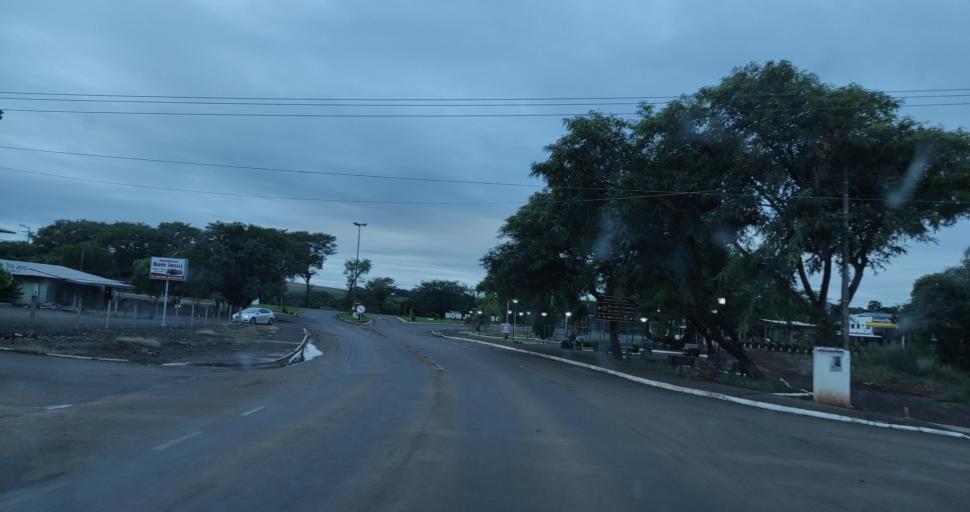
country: BR
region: Santa Catarina
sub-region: Xanxere
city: Xanxere
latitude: -26.7344
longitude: -52.3915
